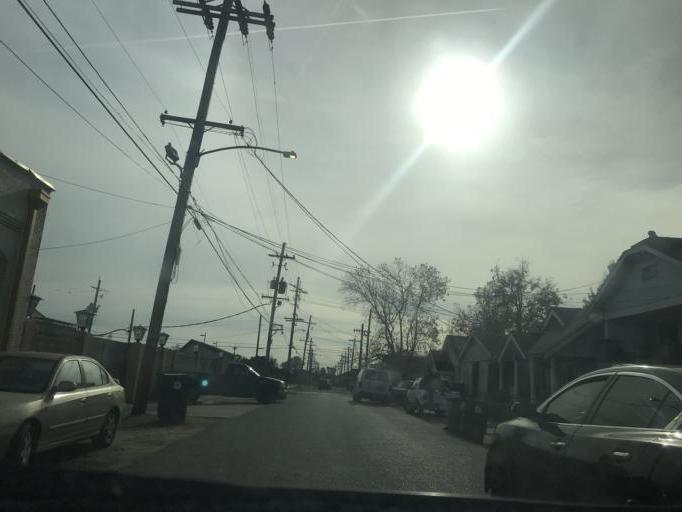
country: US
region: Louisiana
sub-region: Orleans Parish
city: New Orleans
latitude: 29.9595
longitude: -90.1132
